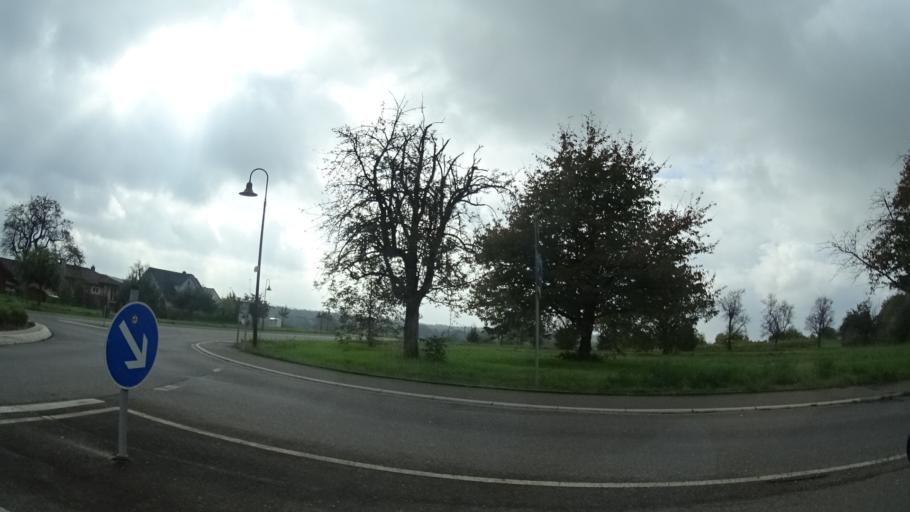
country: DE
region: Baden-Wuerttemberg
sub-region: Karlsruhe Region
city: Malsch
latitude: 49.2433
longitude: 8.6910
